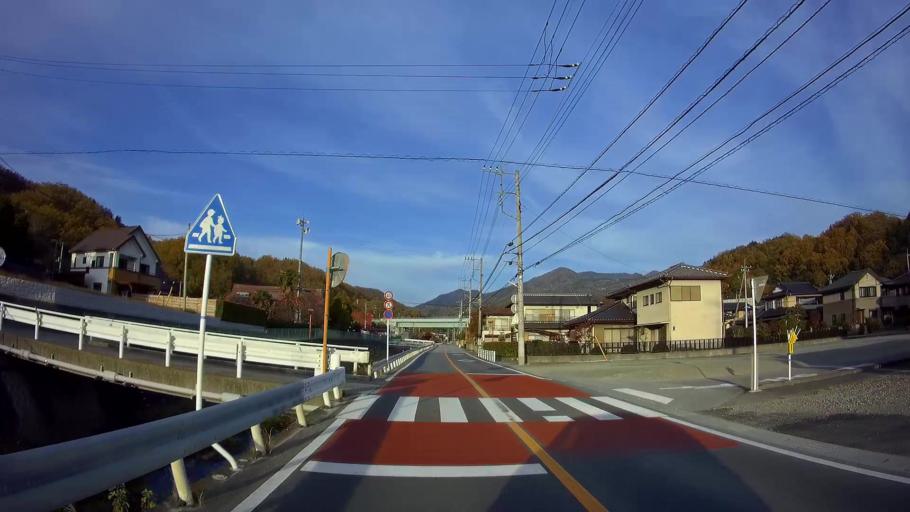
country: JP
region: Yamanashi
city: Ryuo
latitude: 35.5006
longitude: 138.4669
